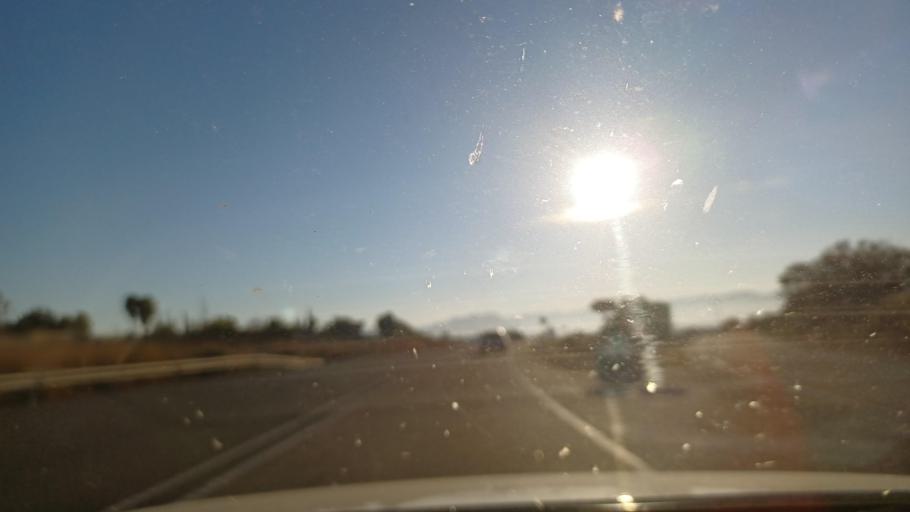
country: ES
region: Valencia
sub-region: Provincia de Valencia
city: Llosa de Ranes
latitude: 39.0178
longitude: -0.5523
